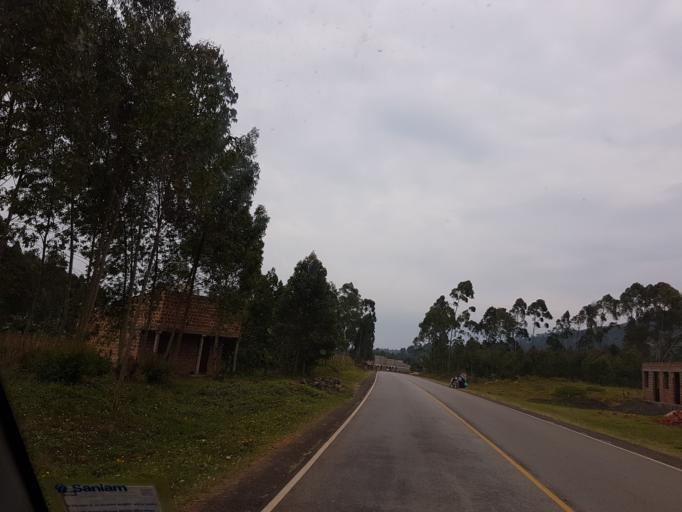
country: UG
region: Western Region
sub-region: Kisoro District
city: Kisoro
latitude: -1.3104
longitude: 29.7208
